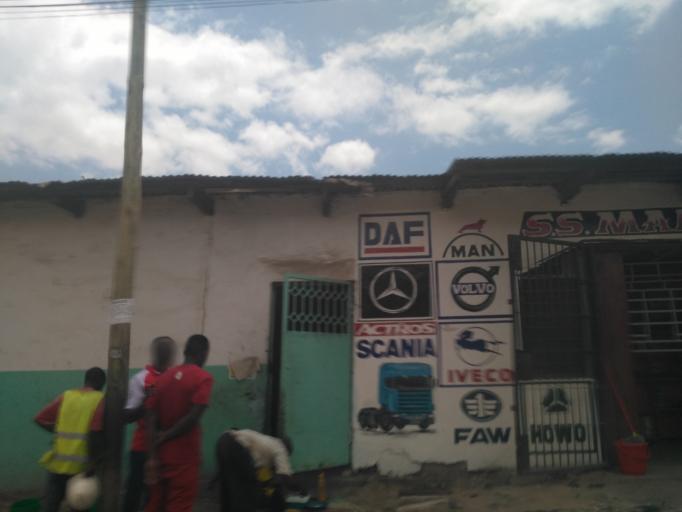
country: TZ
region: Dar es Salaam
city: Dar es Salaam
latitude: -6.8553
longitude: 39.2906
